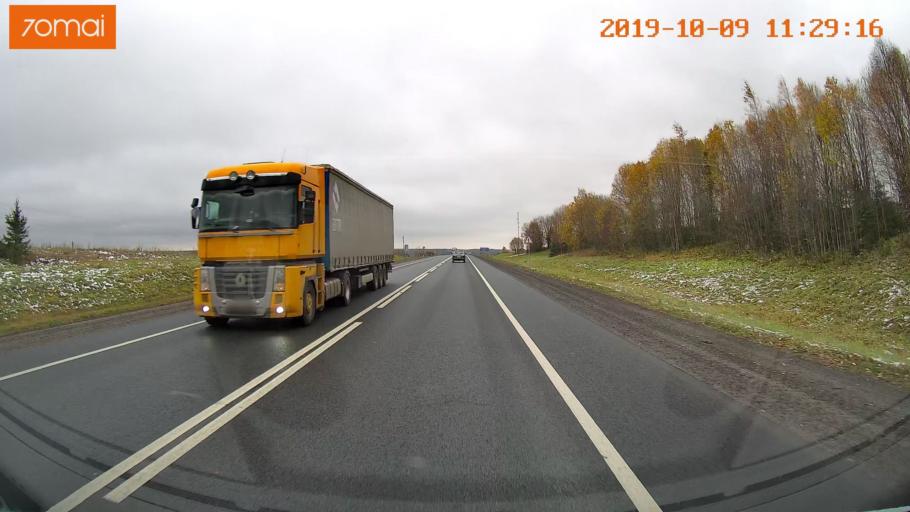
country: RU
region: Vologda
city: Vologda
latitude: 59.0635
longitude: 40.0503
